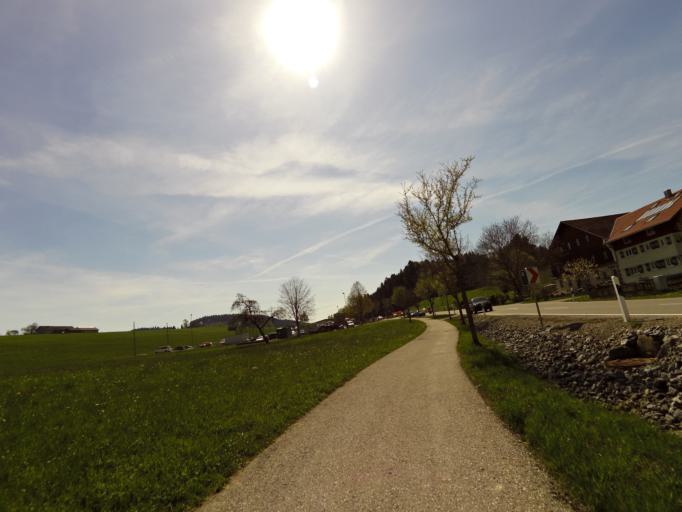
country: DE
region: Bavaria
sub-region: Swabia
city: Oberreute
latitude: 47.5947
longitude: 9.9524
